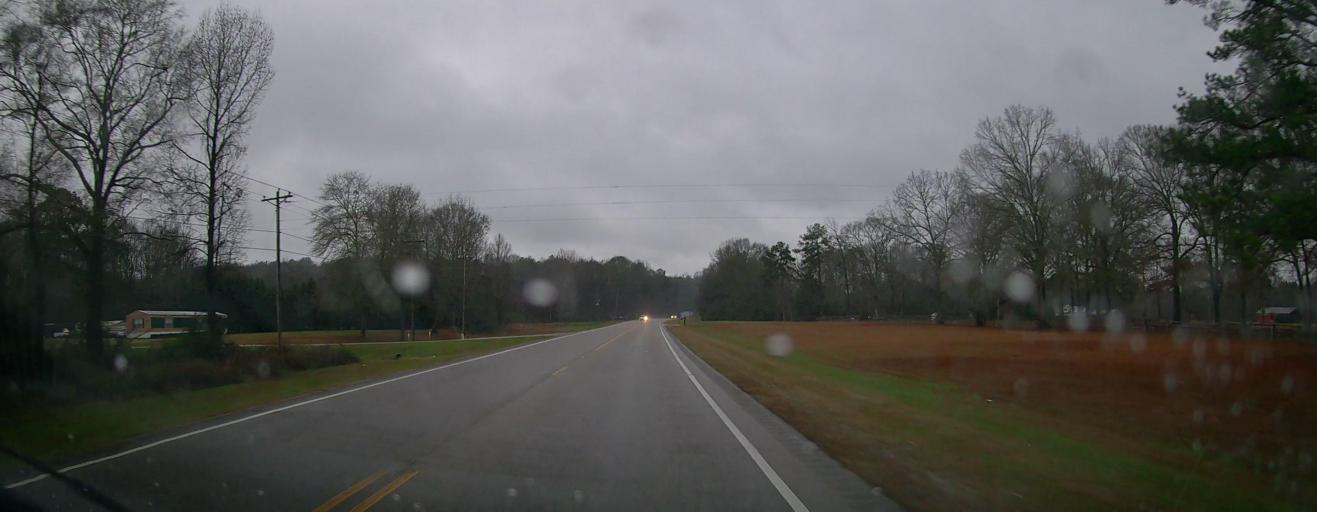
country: US
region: Alabama
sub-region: Autauga County
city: Prattville
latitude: 32.4965
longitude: -86.5806
